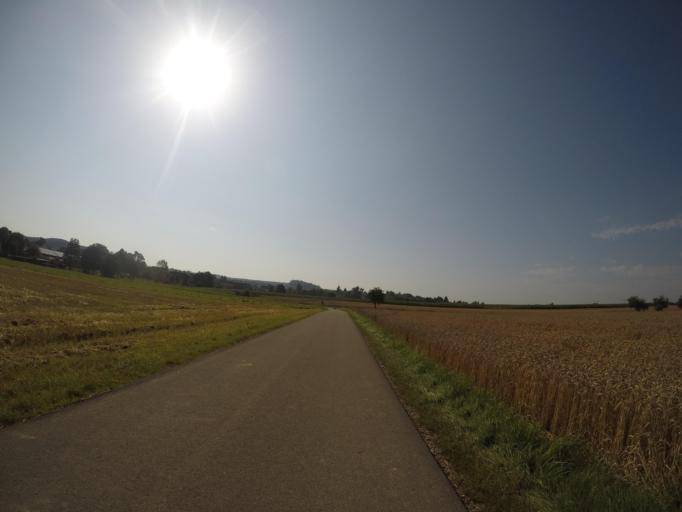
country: DE
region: Baden-Wuerttemberg
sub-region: Tuebingen Region
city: Wain
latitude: 48.1975
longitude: 10.0180
